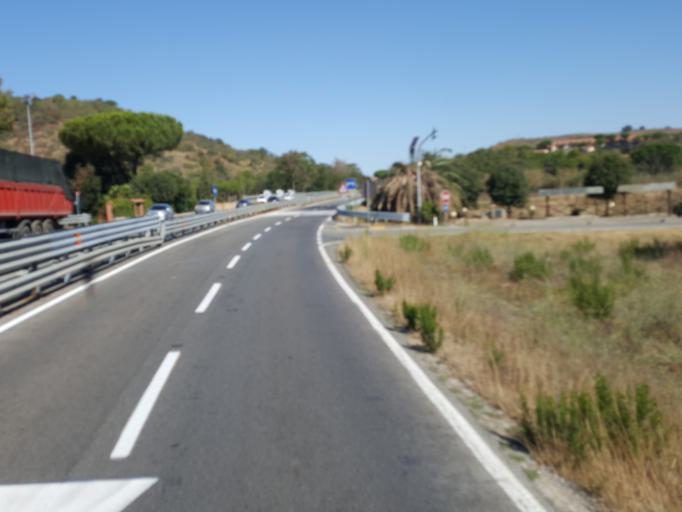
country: IT
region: Tuscany
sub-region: Provincia di Grosseto
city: Fonteblanda
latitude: 42.5476
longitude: 11.1750
